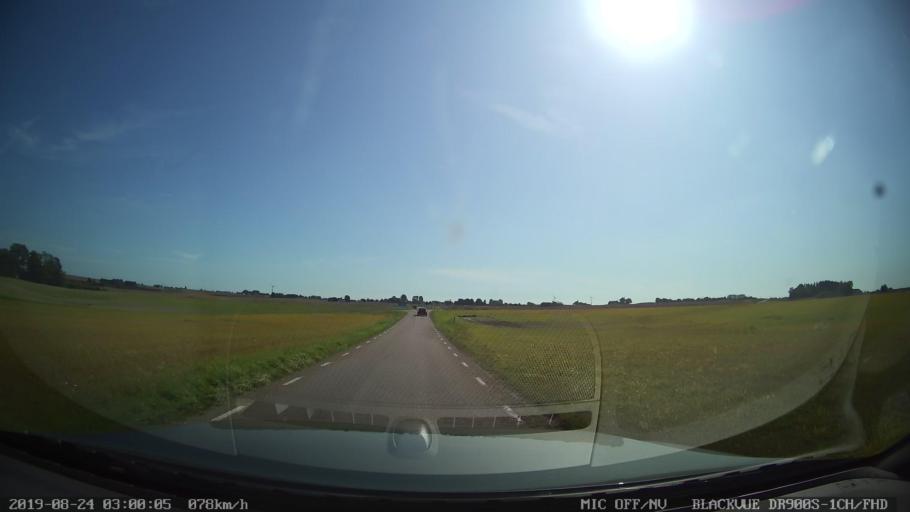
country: SE
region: Skane
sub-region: Skurups Kommun
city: Skurup
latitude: 55.4607
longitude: 13.4291
